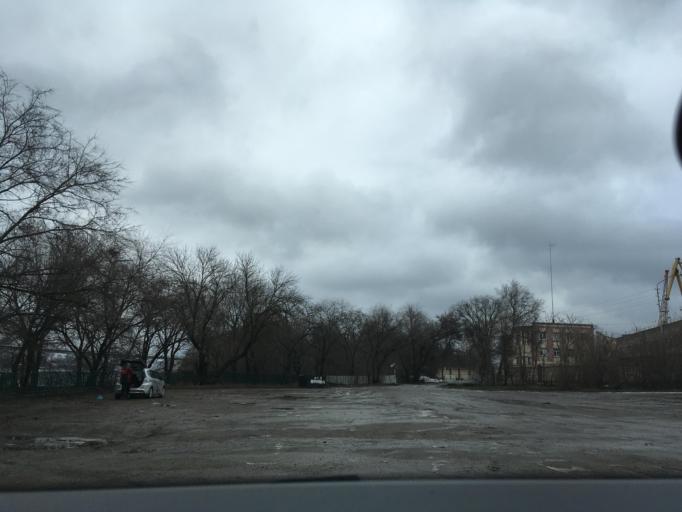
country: RU
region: Rostov
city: Rostov-na-Donu
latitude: 47.2113
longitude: 39.7120
